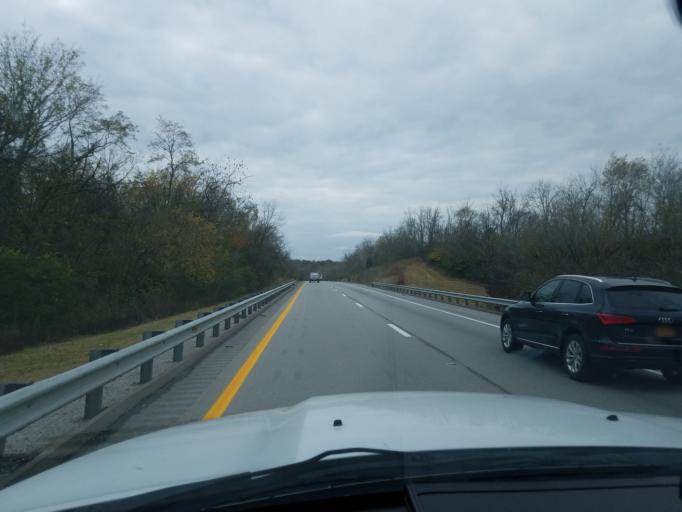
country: US
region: Kentucky
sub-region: Trimble County
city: Providence
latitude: 38.4870
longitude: -85.2641
